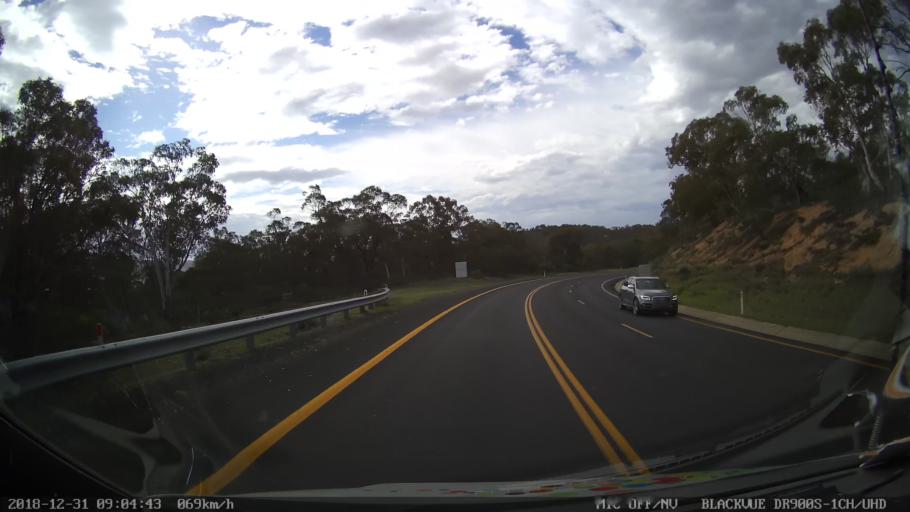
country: AU
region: New South Wales
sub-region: Snowy River
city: Jindabyne
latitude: -36.3565
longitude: 148.5892
